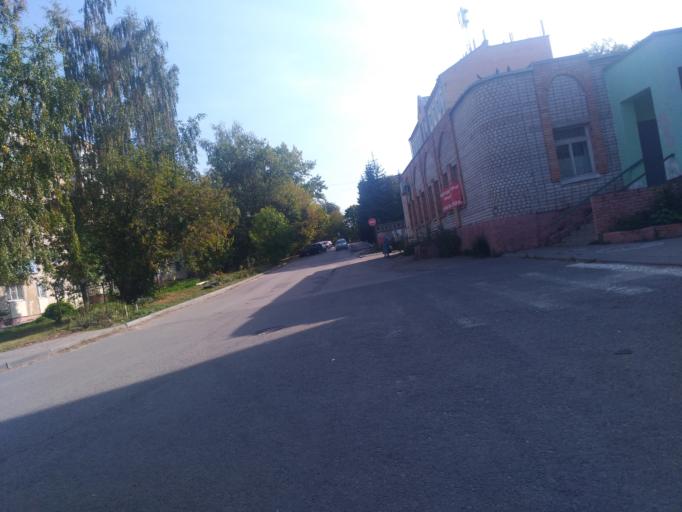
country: RU
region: Kaluga
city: Kaluga
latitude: 54.5316
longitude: 36.2537
